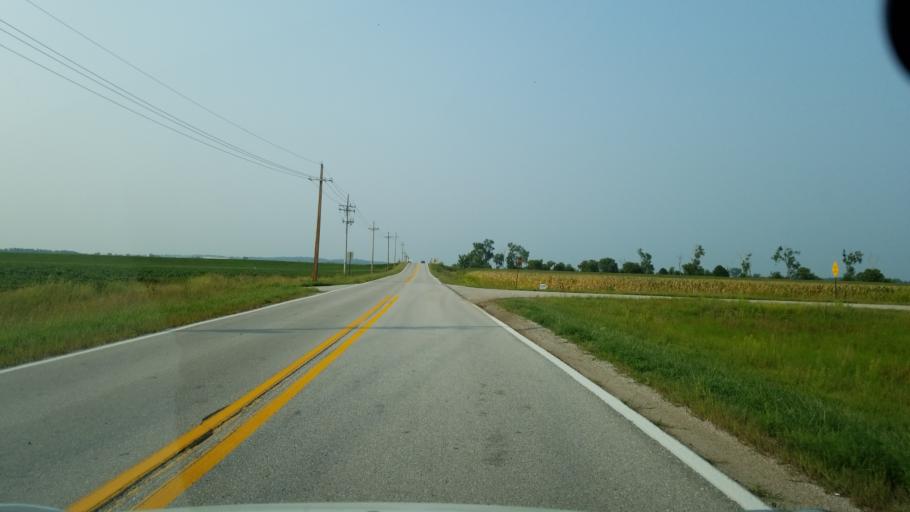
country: US
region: Nebraska
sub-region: Sarpy County
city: Offutt Air Force Base
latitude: 41.0789
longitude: -95.8898
